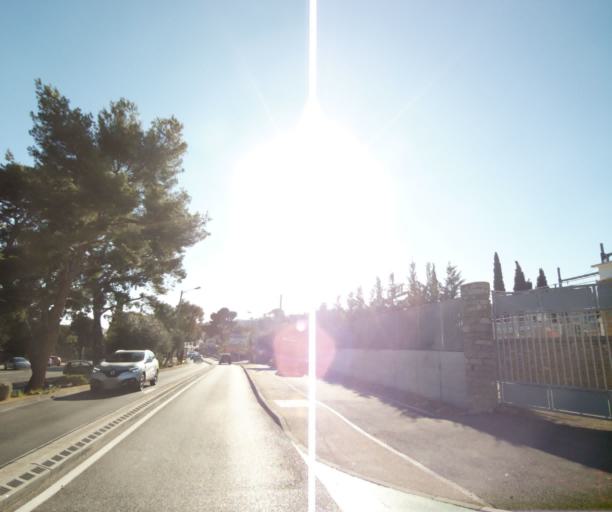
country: FR
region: Provence-Alpes-Cote d'Azur
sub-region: Departement des Bouches-du-Rhone
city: La Ciotat
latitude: 43.1857
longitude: 5.5998
